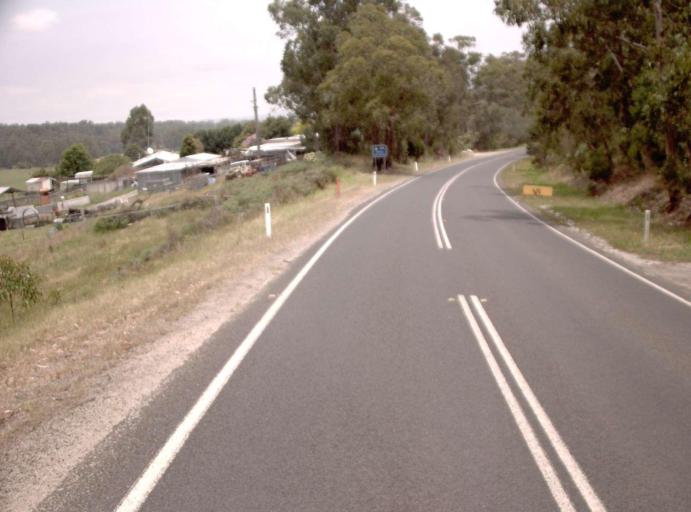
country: AU
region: Victoria
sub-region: Latrobe
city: Traralgon
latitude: -38.4575
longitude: 146.7354
